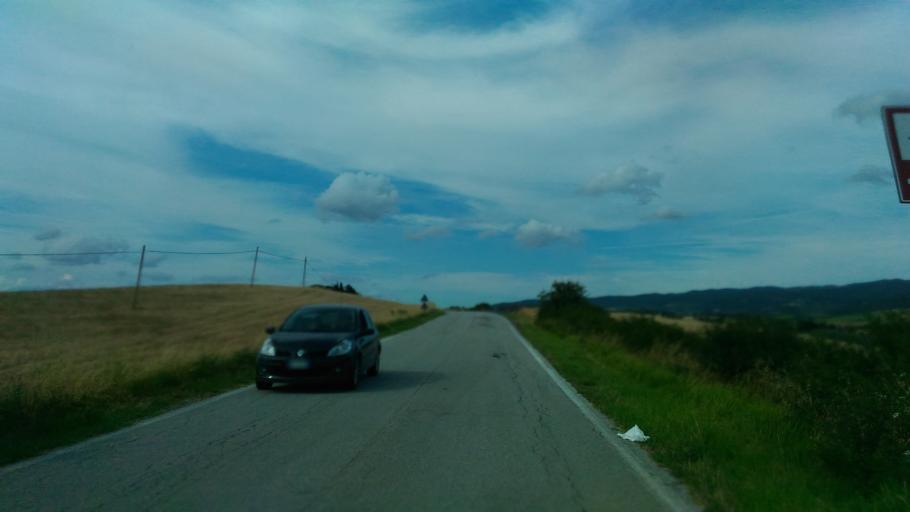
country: IT
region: Tuscany
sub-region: Province of Pisa
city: Orciano Pisano
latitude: 43.4474
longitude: 10.5106
